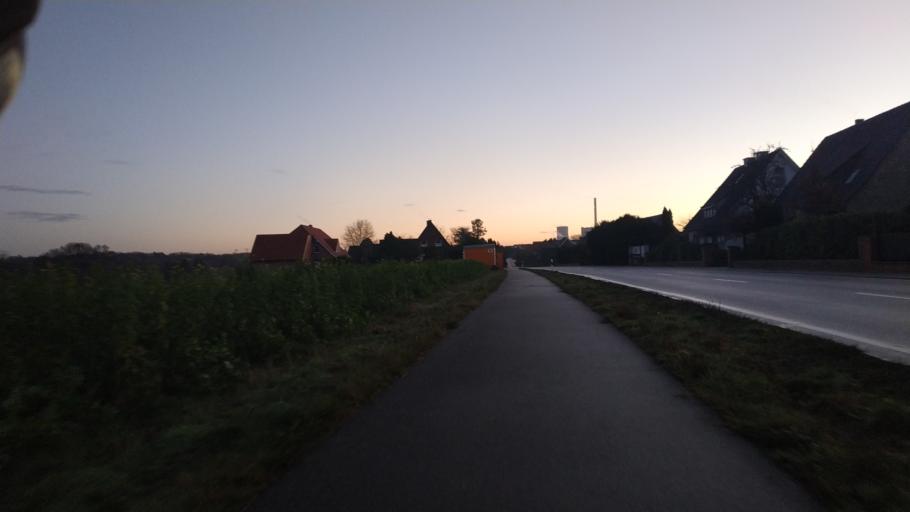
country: DE
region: North Rhine-Westphalia
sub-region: Regierungsbezirk Munster
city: Mettingen
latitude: 52.3156
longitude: 7.7532
